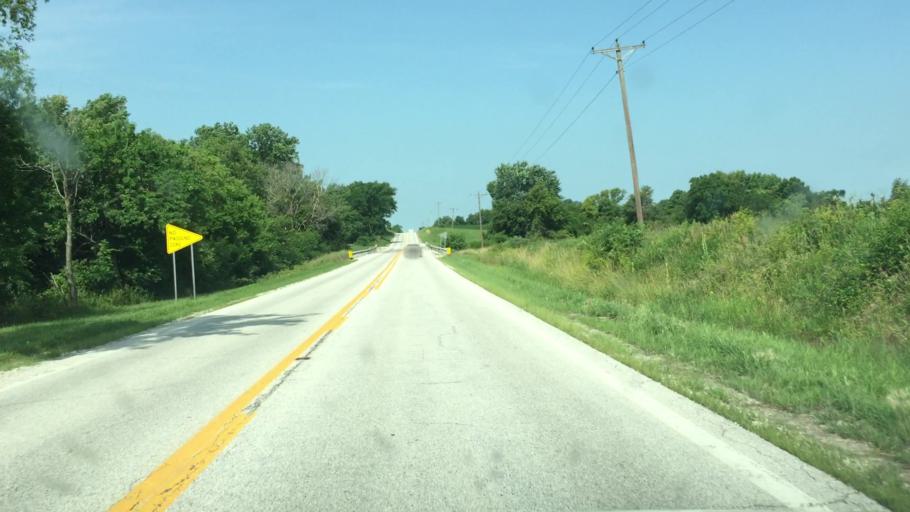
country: US
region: Illinois
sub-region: Hancock County
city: Nauvoo
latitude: 40.5515
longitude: -91.3138
